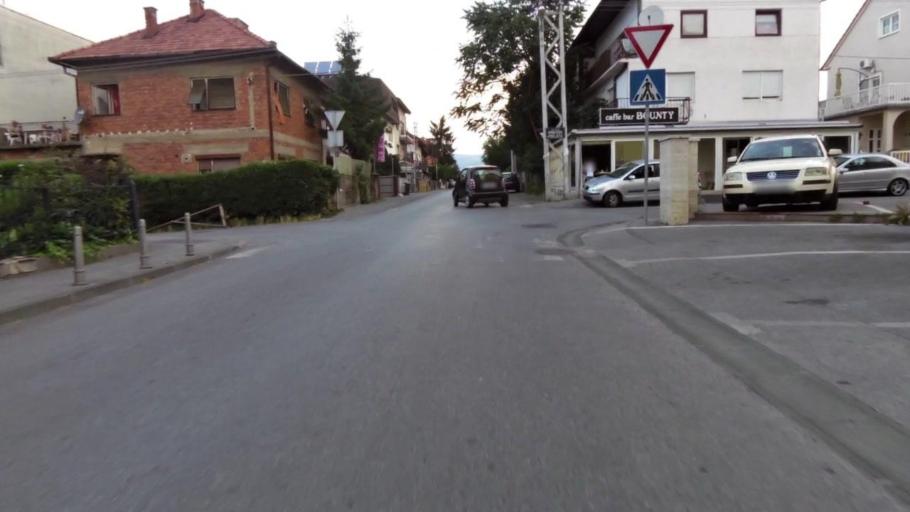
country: HR
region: Grad Zagreb
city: Dubrava
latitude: 45.8259
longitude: 16.0419
